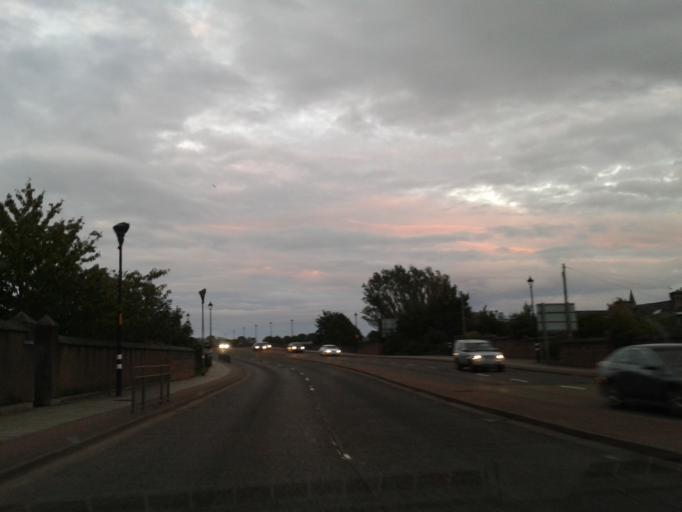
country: GB
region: Scotland
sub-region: Highland
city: Inverness
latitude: 57.4807
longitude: -4.2367
